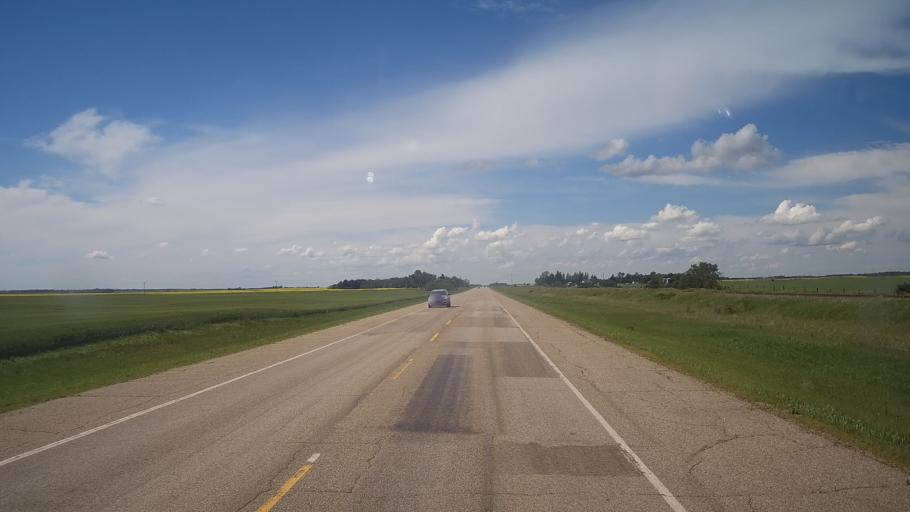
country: CA
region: Saskatchewan
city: Yorkton
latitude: 51.0866
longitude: -102.2551
